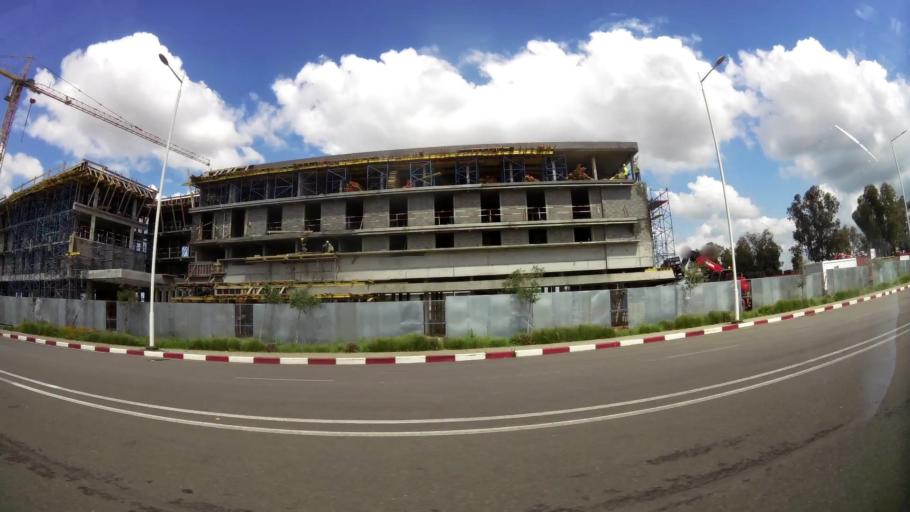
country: MA
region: Chaouia-Ouardigha
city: Nouaseur
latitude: 33.3727
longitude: -7.5670
